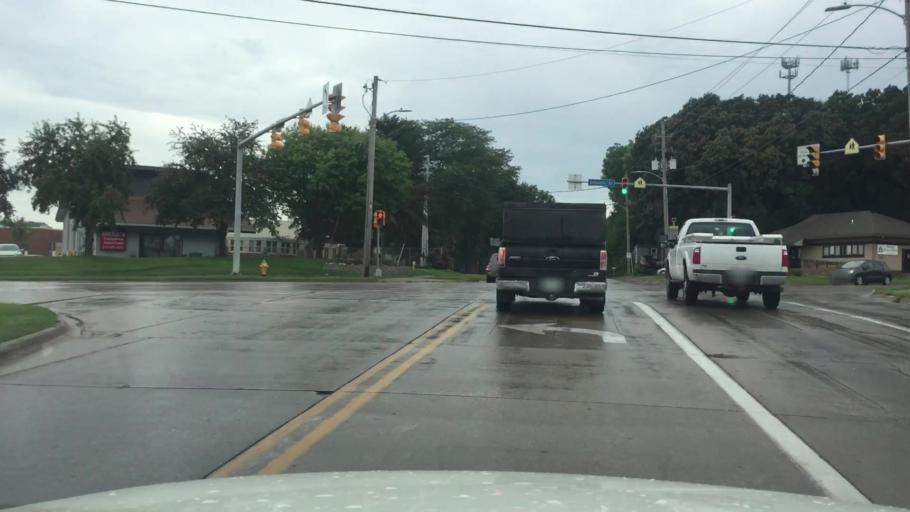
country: US
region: Iowa
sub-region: Polk County
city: Des Moines
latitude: 41.5553
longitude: -93.5983
